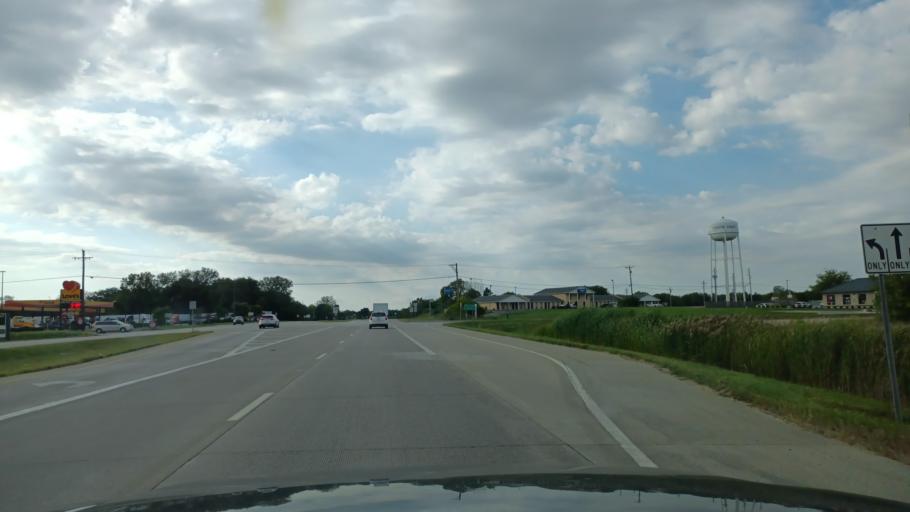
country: US
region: Ohio
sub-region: Fayette County
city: Jeffersonville
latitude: 39.6208
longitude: -83.6104
